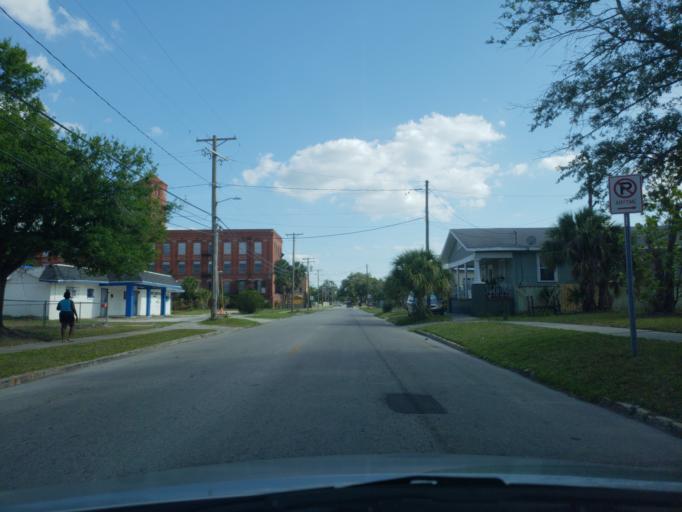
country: US
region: Florida
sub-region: Hillsborough County
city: Tampa
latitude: 27.9629
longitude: -82.4808
